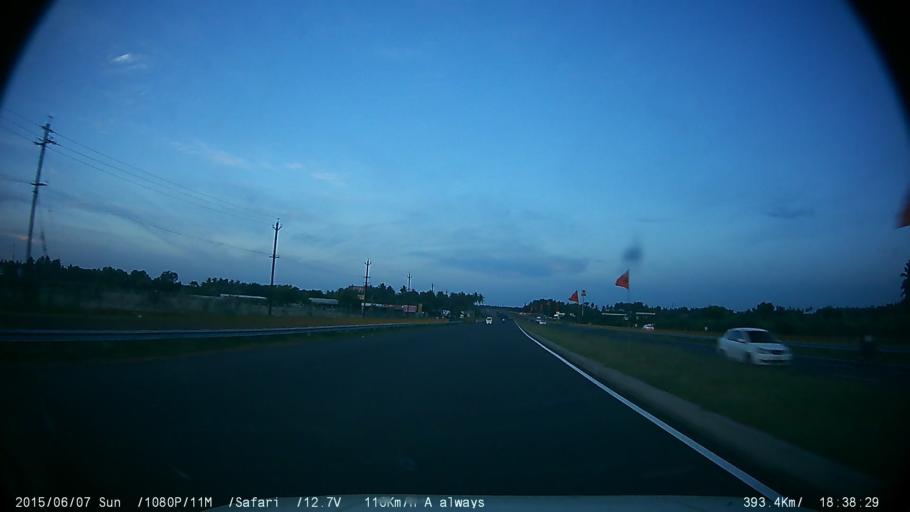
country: IN
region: Tamil Nadu
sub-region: Tiruppur
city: Avinashi
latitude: 11.2033
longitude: 77.3321
